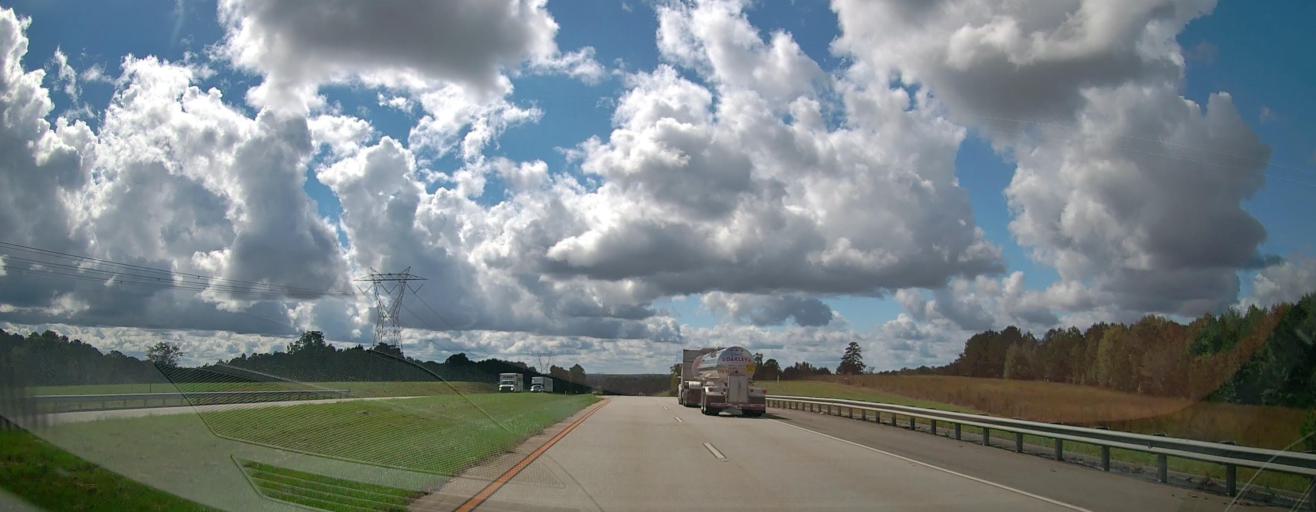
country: US
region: Georgia
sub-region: Jones County
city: Gray
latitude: 33.0230
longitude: -83.5557
